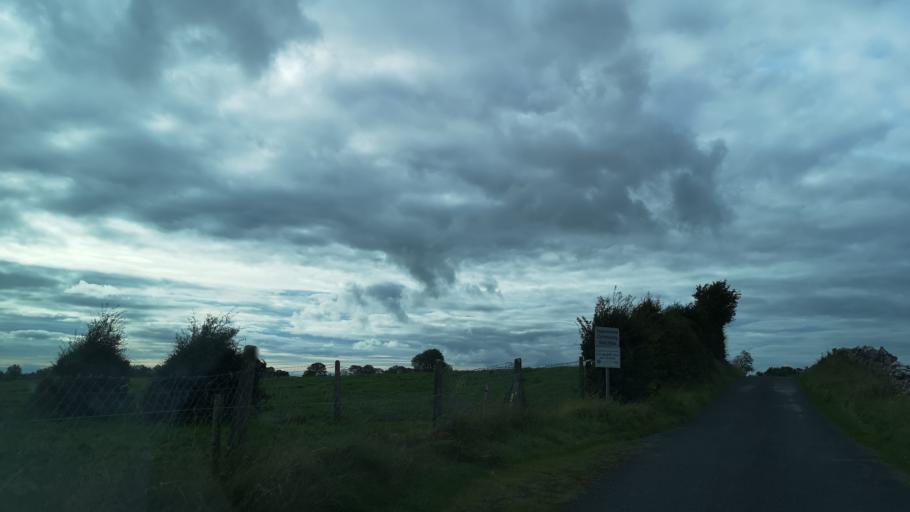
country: IE
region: Connaught
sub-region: County Galway
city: Ballinasloe
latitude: 53.3763
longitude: -8.1710
